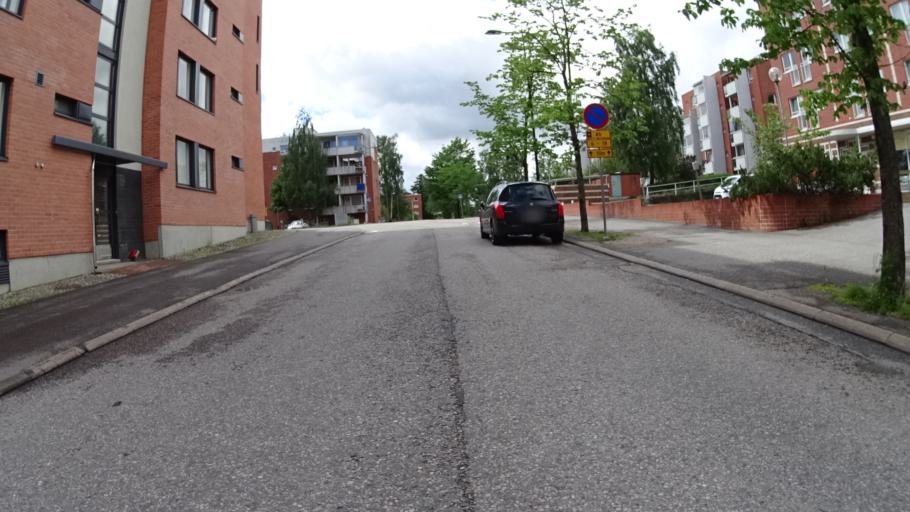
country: FI
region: Uusimaa
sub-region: Helsinki
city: Teekkarikylae
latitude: 60.2250
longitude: 24.8200
